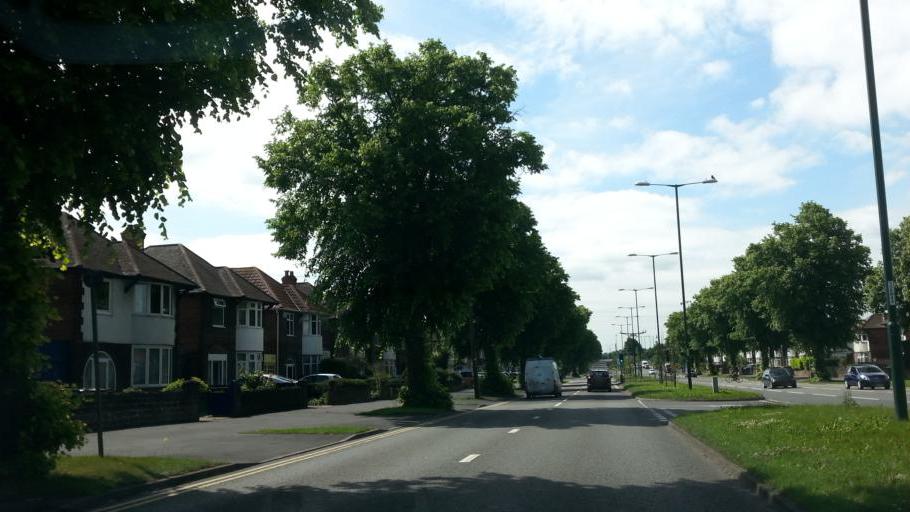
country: GB
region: England
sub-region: Nottingham
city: Nottingham
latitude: 52.9637
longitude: -1.1908
